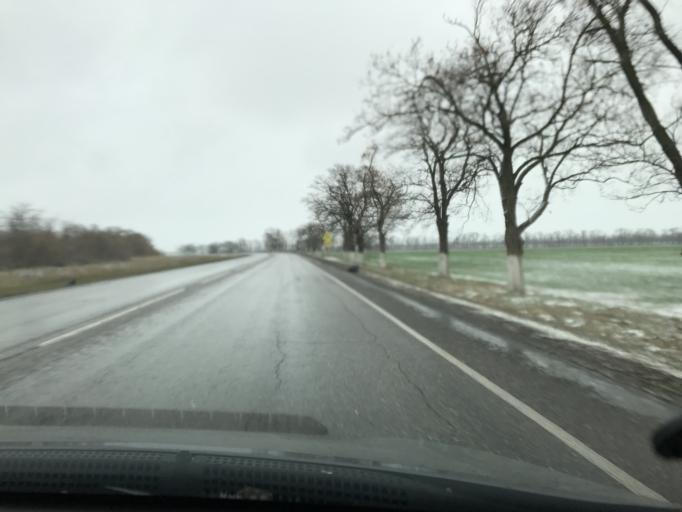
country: RU
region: Rostov
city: Zernograd
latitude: 46.8187
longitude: 40.2610
